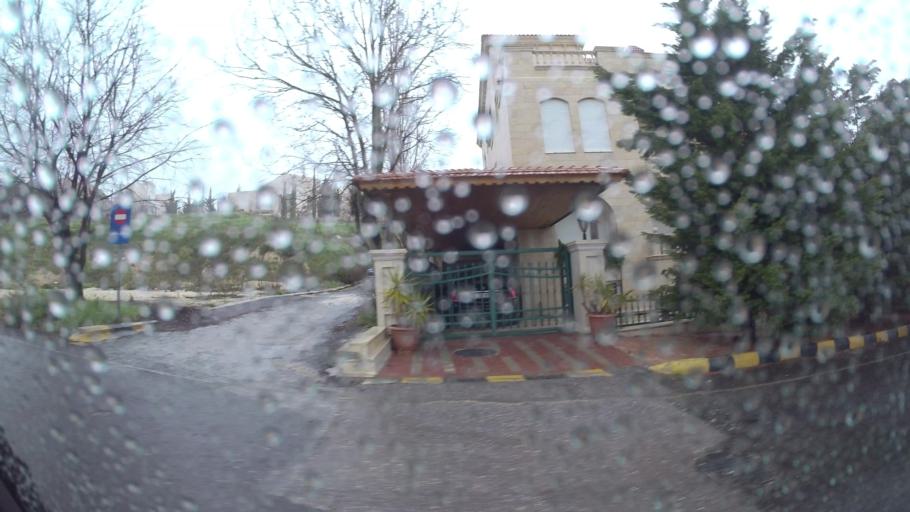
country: JO
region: Amman
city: Al Jubayhah
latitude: 32.0080
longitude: 35.8277
